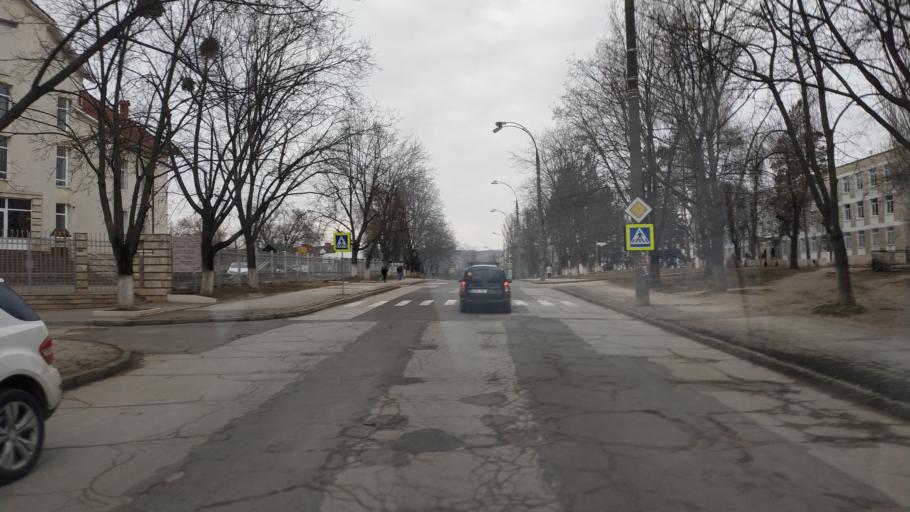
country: MD
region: Chisinau
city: Vatra
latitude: 47.0280
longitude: 28.7873
